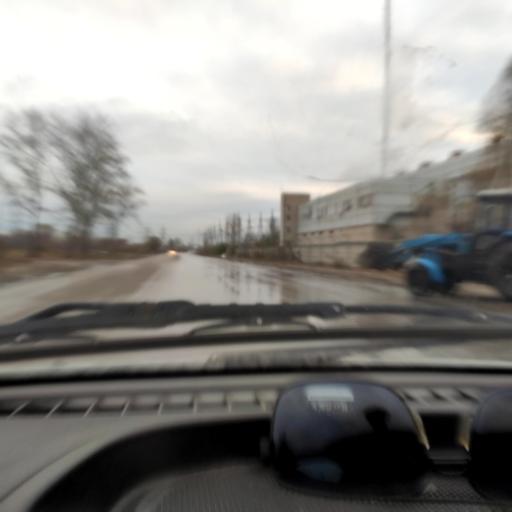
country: RU
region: Samara
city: Zhigulevsk
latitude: 53.5125
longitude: 49.4634
